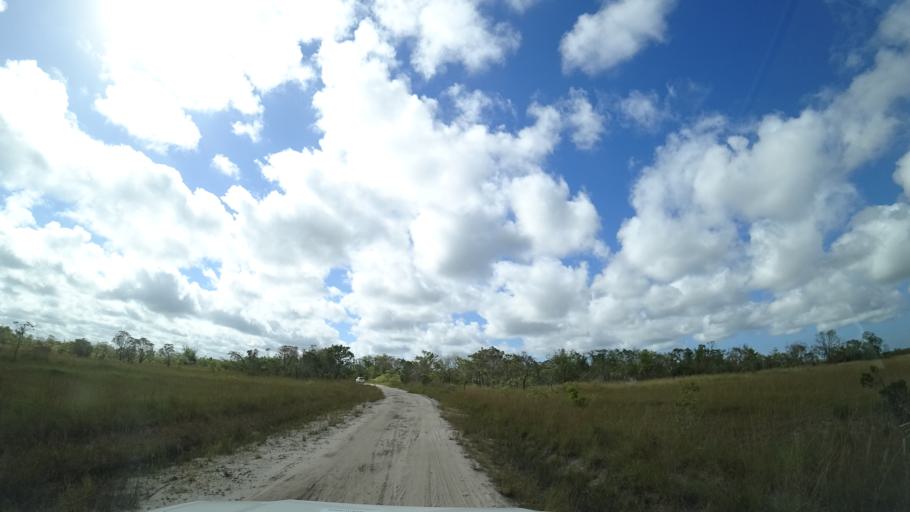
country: MZ
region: Sofala
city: Beira
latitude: -19.6128
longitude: 35.0739
